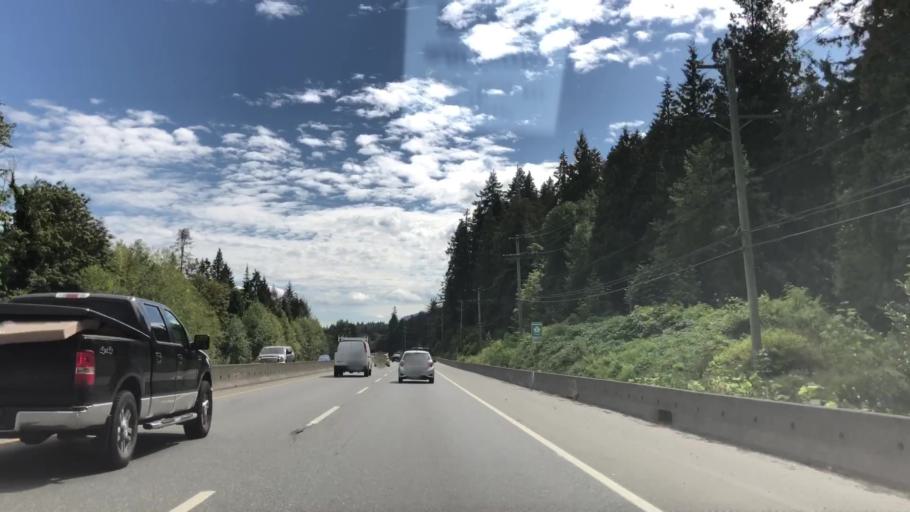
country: CA
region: British Columbia
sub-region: Cowichan Valley Regional District
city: Ladysmith
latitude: 49.0194
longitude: -123.8594
